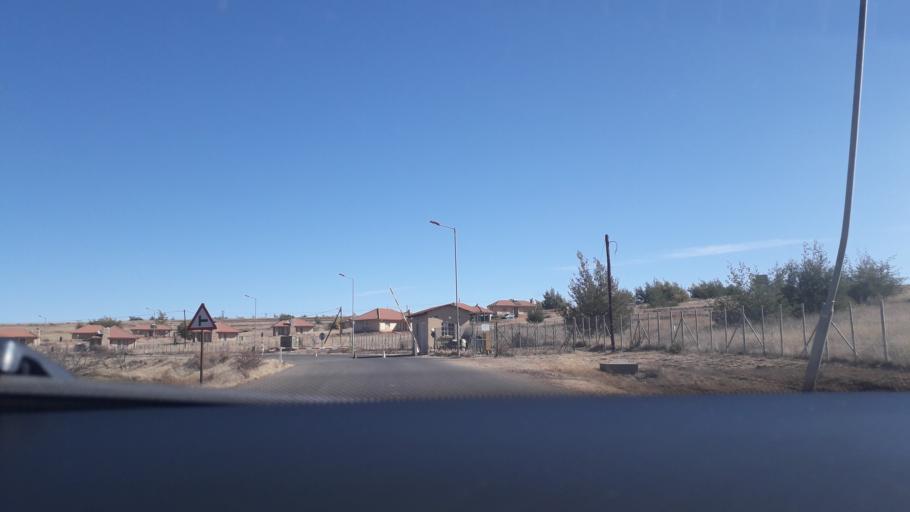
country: LS
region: Berea
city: Teyateyaneng
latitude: -29.3266
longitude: 27.7736
